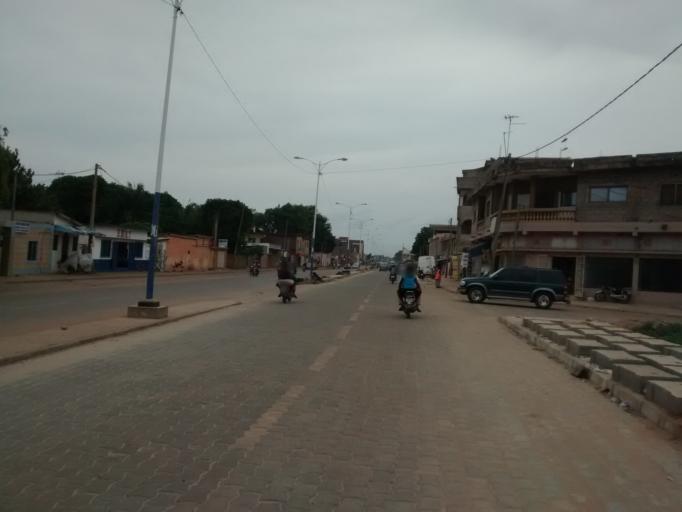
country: TG
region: Maritime
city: Lome
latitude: 6.1751
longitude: 1.1980
